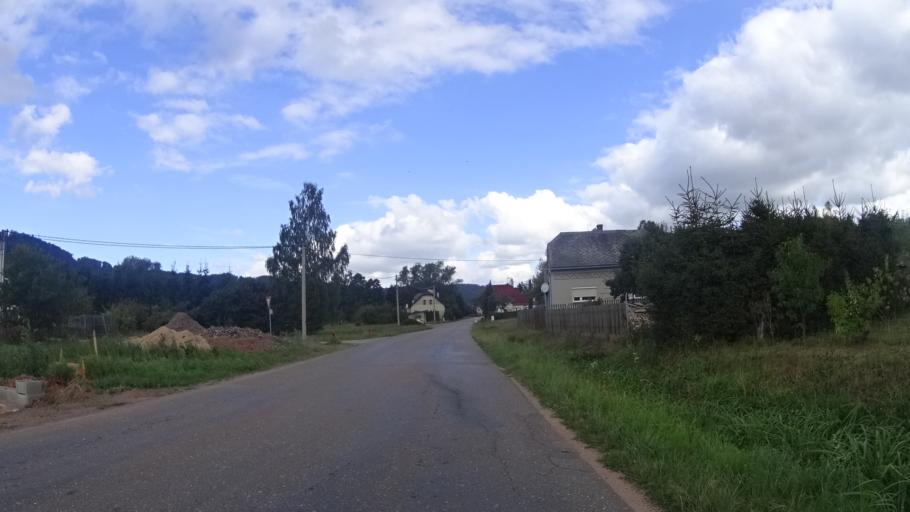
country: CZ
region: Pardubicky
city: Dolni Cermna
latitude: 49.9419
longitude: 16.5230
